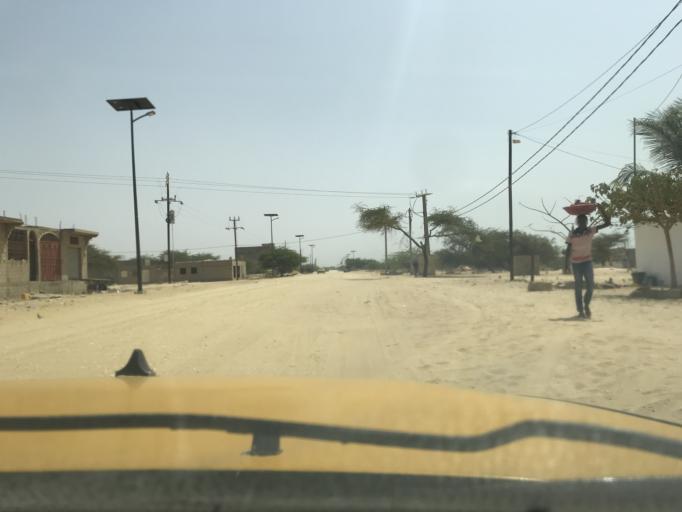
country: SN
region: Saint-Louis
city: Saint-Louis
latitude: 16.0341
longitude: -16.4442
